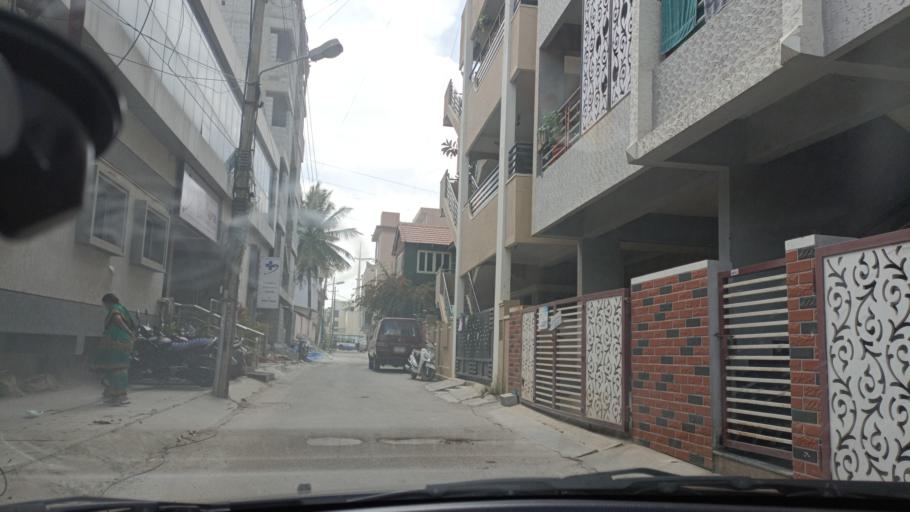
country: IN
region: Karnataka
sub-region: Bangalore Urban
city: Bangalore
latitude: 13.0296
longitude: 77.6324
